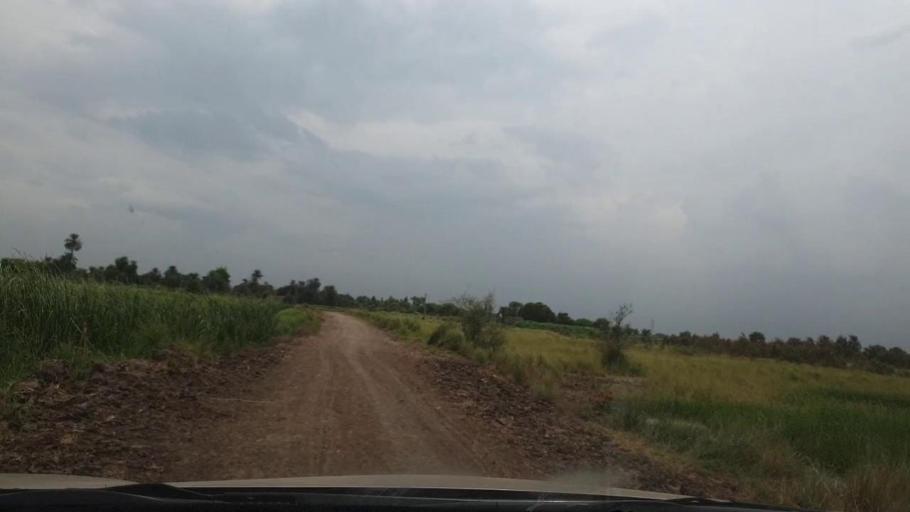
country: PK
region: Sindh
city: Ratodero
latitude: 27.7981
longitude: 68.3129
